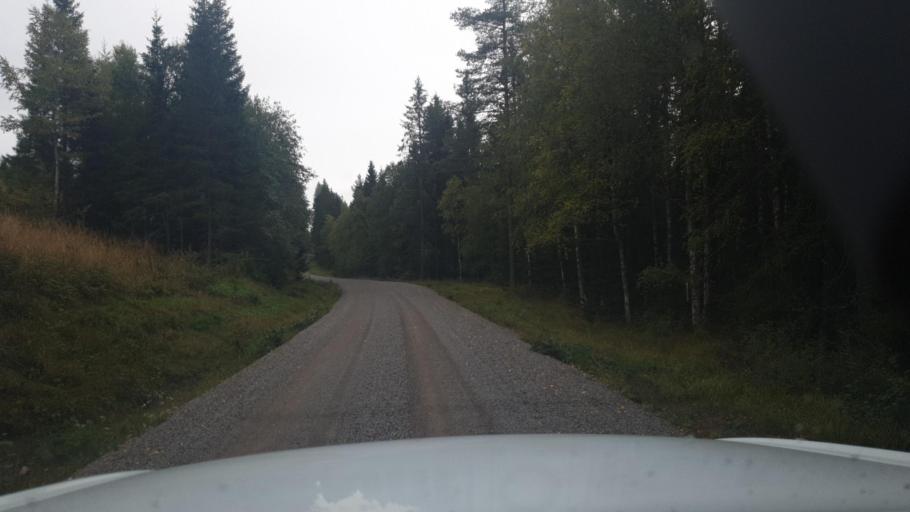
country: SE
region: Vaermland
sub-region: Eda Kommun
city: Charlottenberg
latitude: 60.0563
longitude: 12.6263
